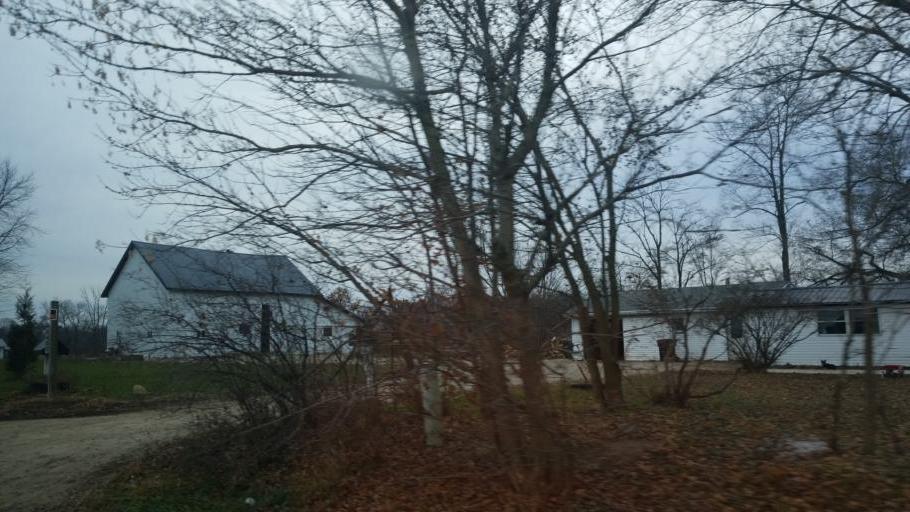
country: US
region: Indiana
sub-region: Adams County
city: Berne
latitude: 40.6680
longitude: -84.8595
